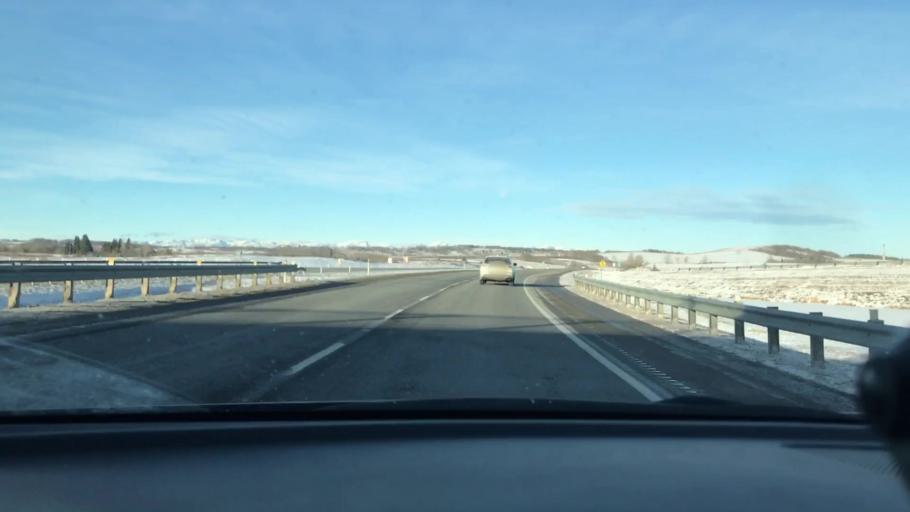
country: CA
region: Alberta
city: Cochrane
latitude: 51.0885
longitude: -114.5361
